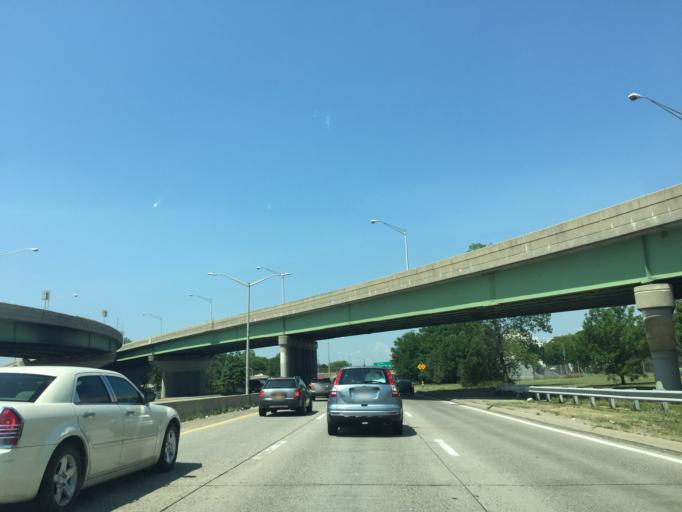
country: US
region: New York
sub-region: Queens County
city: Jamaica
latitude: 40.6666
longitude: -73.7868
